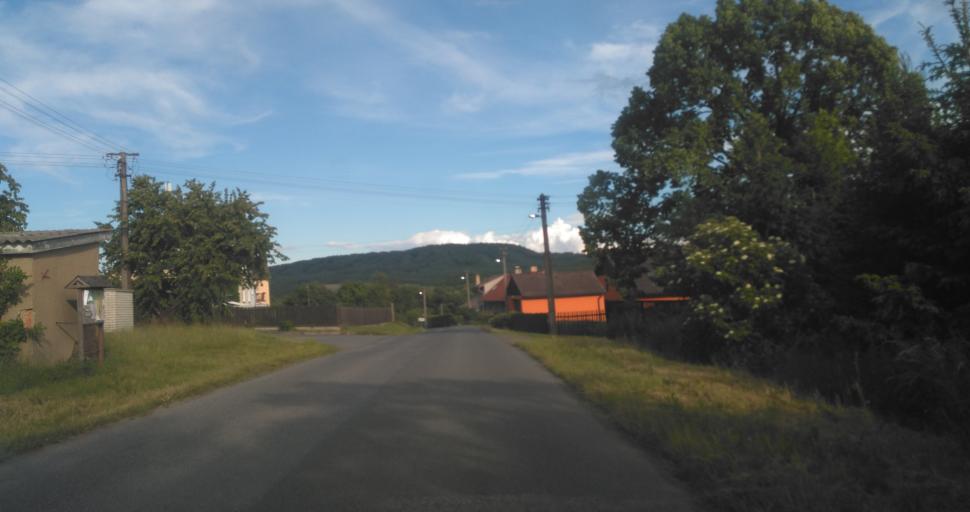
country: CZ
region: Central Bohemia
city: Roztoky
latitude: 49.9792
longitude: 13.8912
